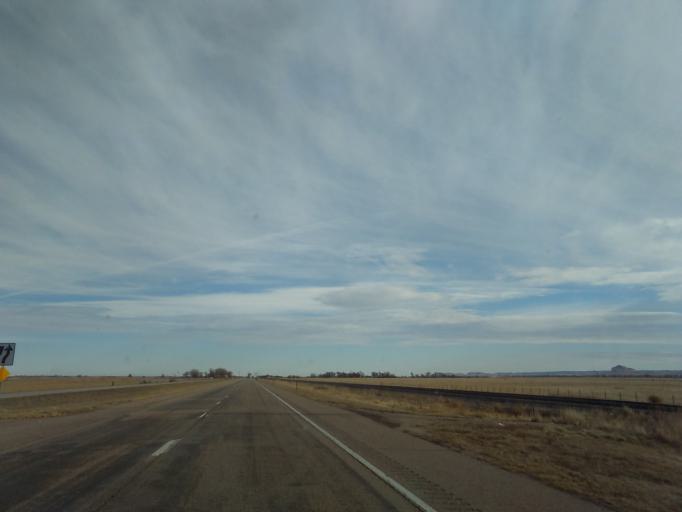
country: US
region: Nebraska
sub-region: Scotts Bluff County
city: Gering
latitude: 41.8251
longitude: -103.5586
